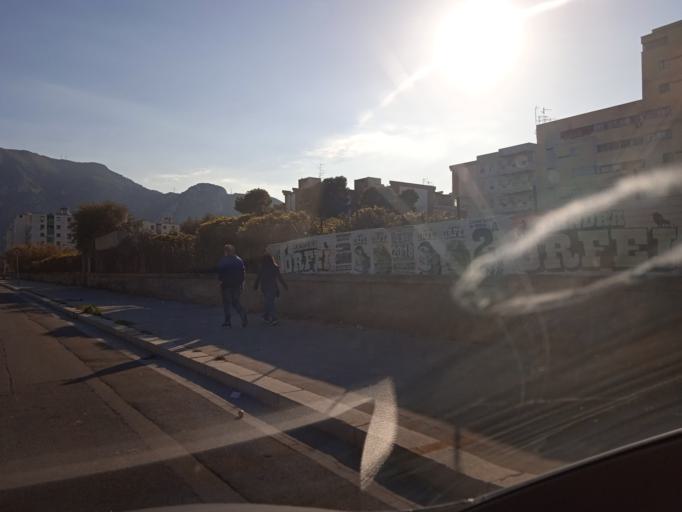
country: IT
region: Sicily
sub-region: Palermo
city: Ciaculli
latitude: 38.0958
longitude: 13.4121
